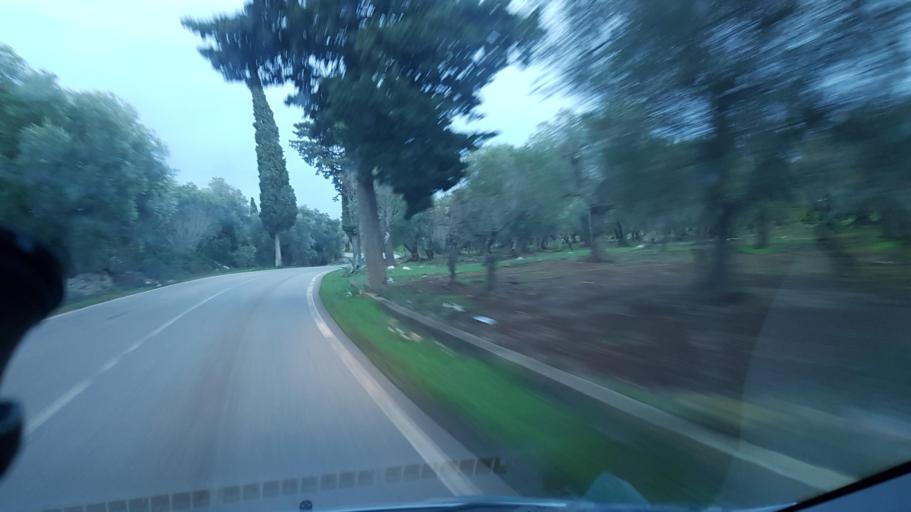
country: IT
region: Apulia
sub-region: Provincia di Brindisi
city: Ceglie Messapica
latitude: 40.6430
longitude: 17.5680
